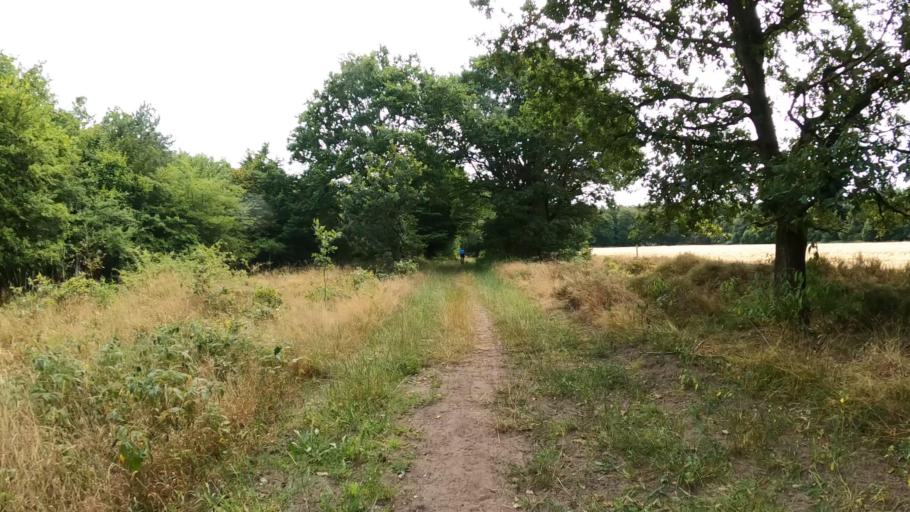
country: DE
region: Schleswig-Holstein
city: Heidmuhlen
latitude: 53.9591
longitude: 10.0993
